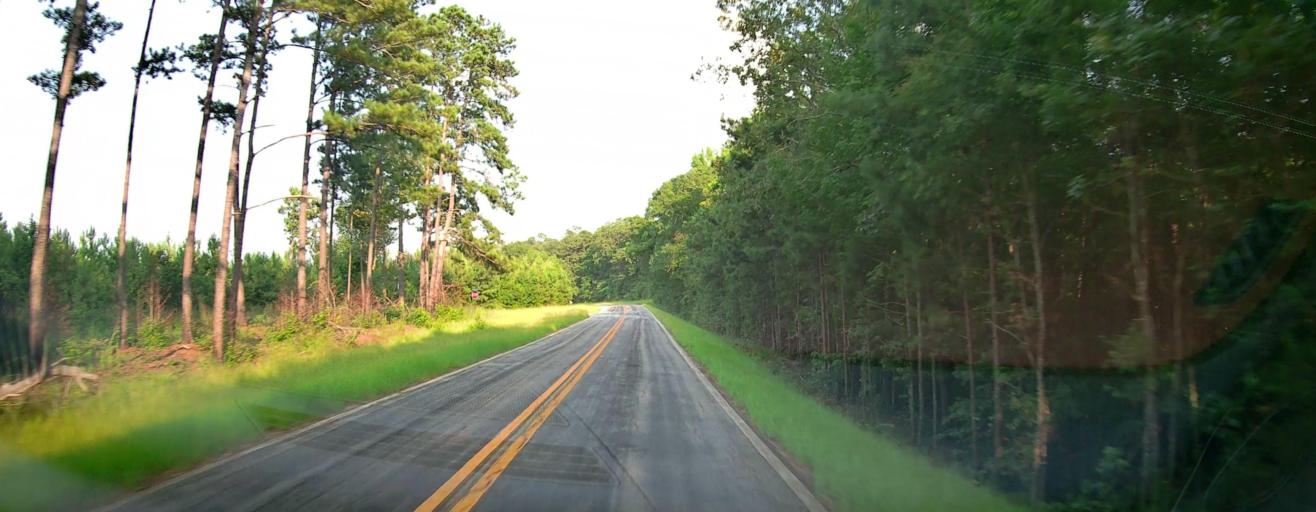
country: US
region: Georgia
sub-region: Jones County
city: Gray
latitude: 33.1130
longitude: -83.6499
